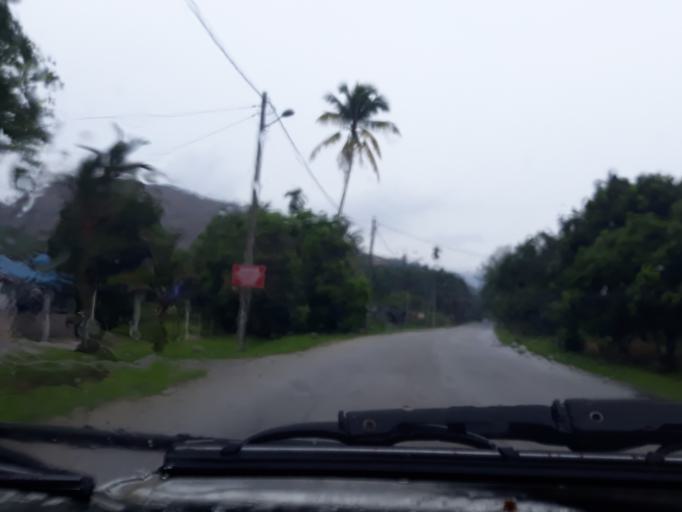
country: MY
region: Kedah
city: Kulim
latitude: 5.2713
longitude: 100.6142
